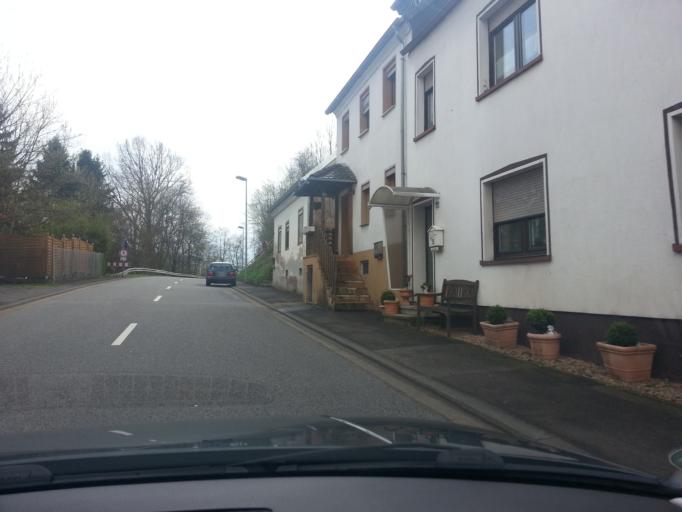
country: DE
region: Saarland
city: Homburg
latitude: 49.2877
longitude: 7.3097
